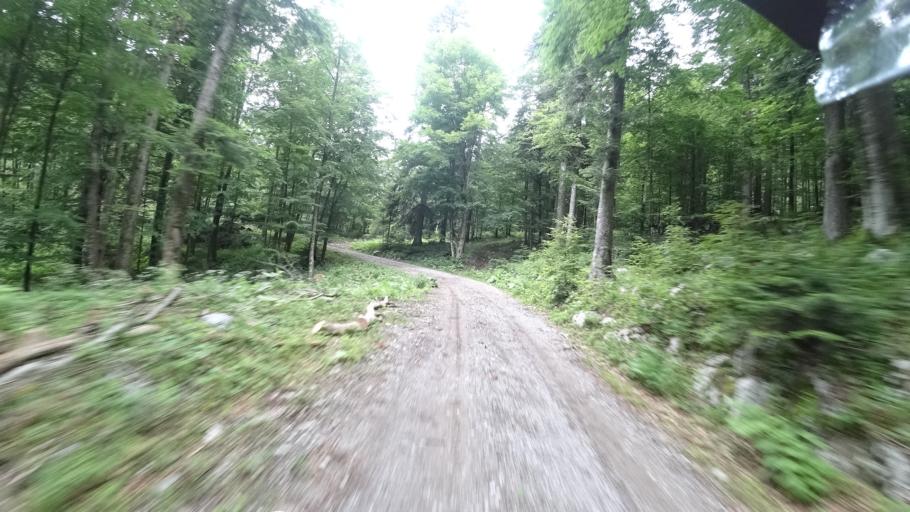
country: HR
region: Primorsko-Goranska
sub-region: Grad Delnice
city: Delnice
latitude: 45.3092
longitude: 14.7644
